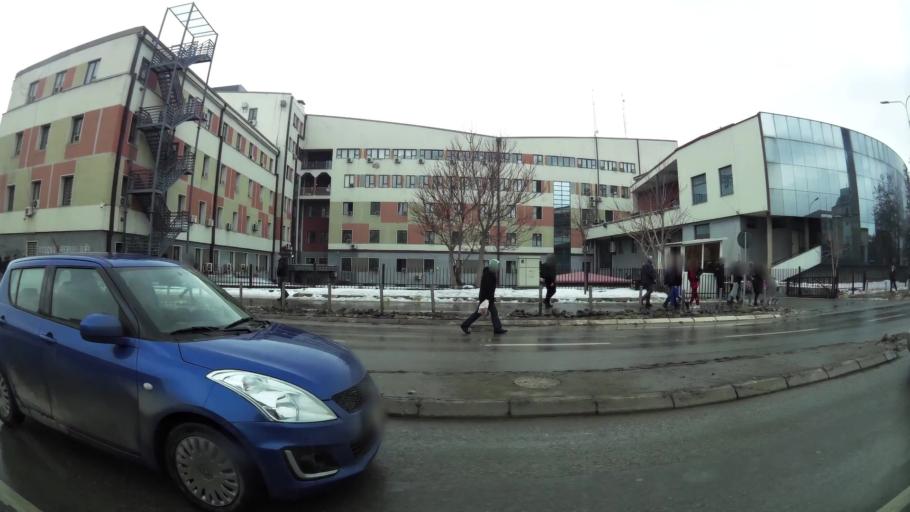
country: XK
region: Pristina
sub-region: Komuna e Prishtines
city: Pristina
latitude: 42.6649
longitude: 21.1652
